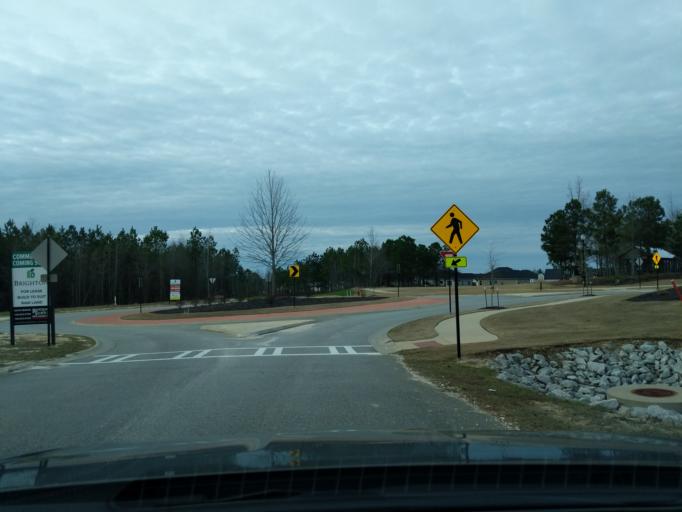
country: US
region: Georgia
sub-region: Columbia County
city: Grovetown
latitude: 33.4665
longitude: -82.2000
